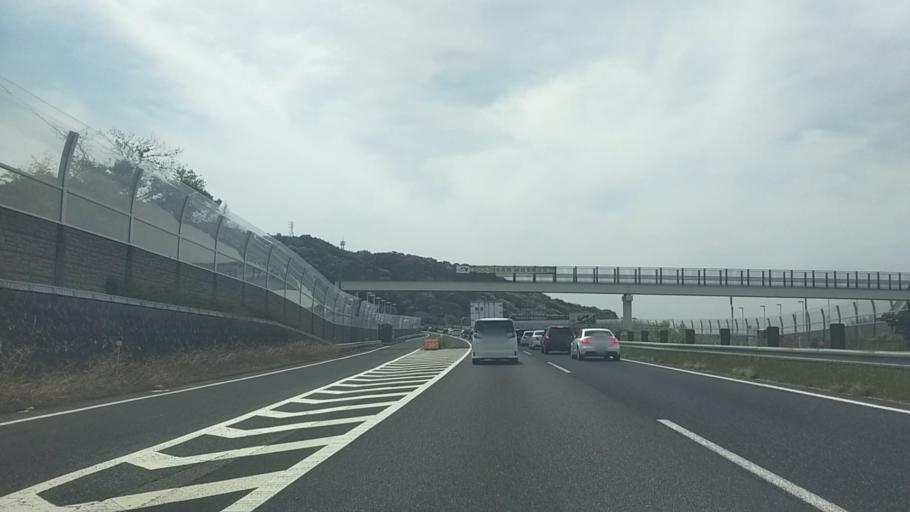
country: JP
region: Aichi
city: Shinshiro
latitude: 34.8176
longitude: 137.5510
